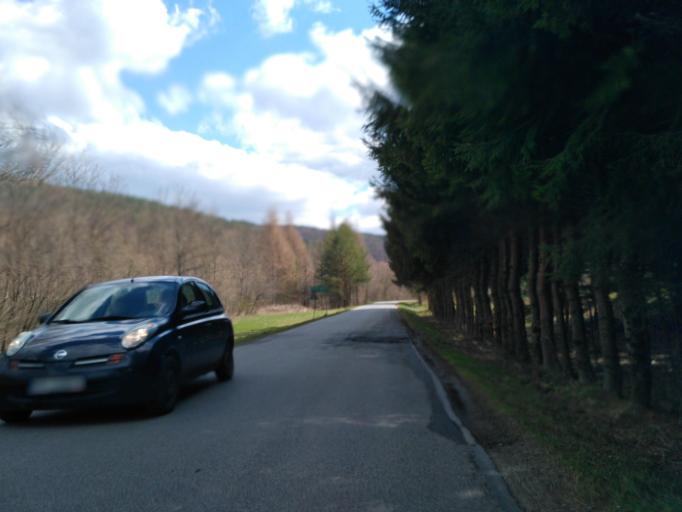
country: PL
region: Subcarpathian Voivodeship
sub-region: Powiat sanocki
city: Tyrawa Woloska
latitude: 49.5946
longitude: 22.3299
